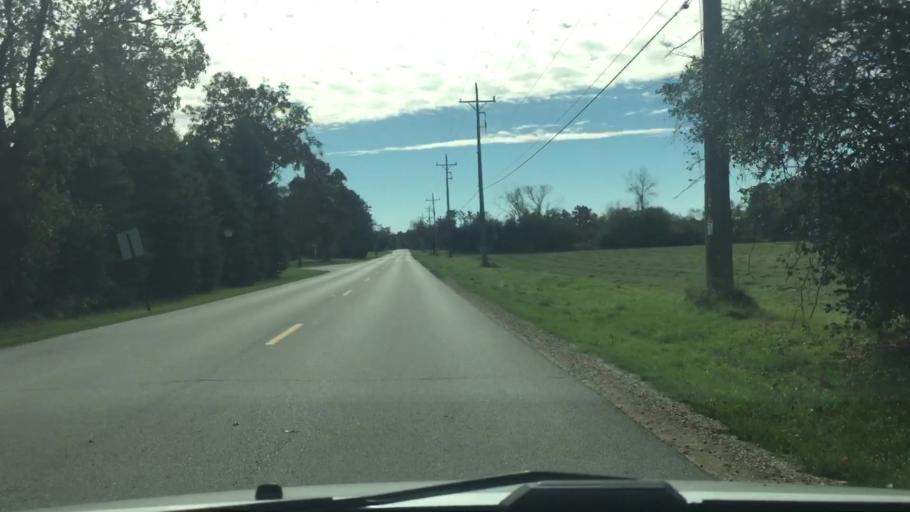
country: US
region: Wisconsin
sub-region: Waukesha County
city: Dousman
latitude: 43.0383
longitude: -88.4838
